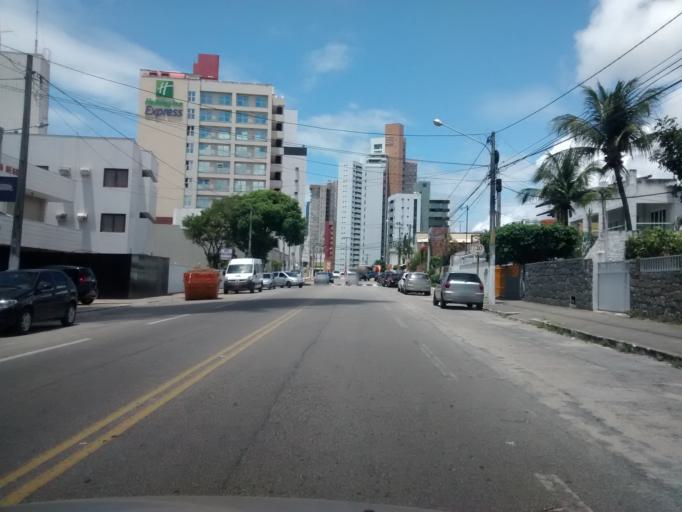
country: BR
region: Rio Grande do Norte
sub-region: Natal
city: Natal
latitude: -5.8720
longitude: -35.1812
